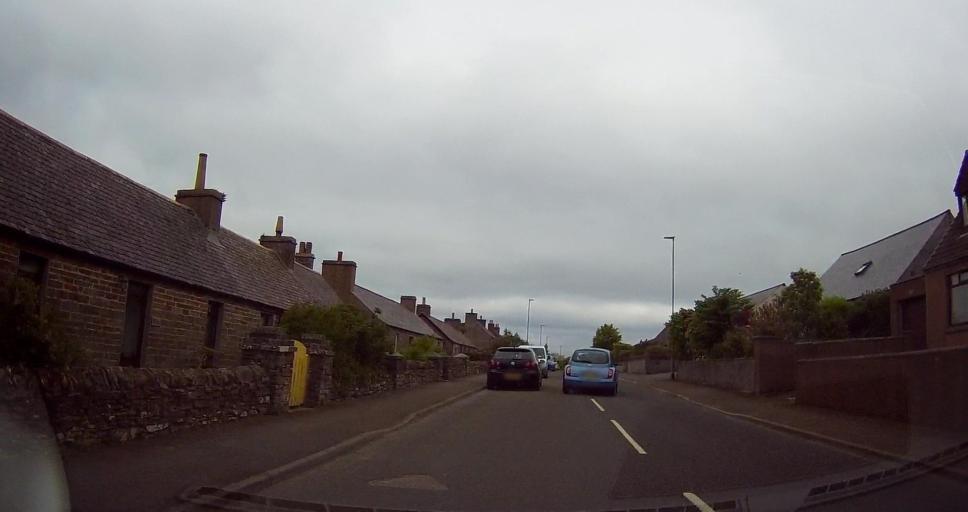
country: GB
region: Scotland
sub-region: Orkney Islands
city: Kirkwall
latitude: 58.9739
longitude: -2.9534
